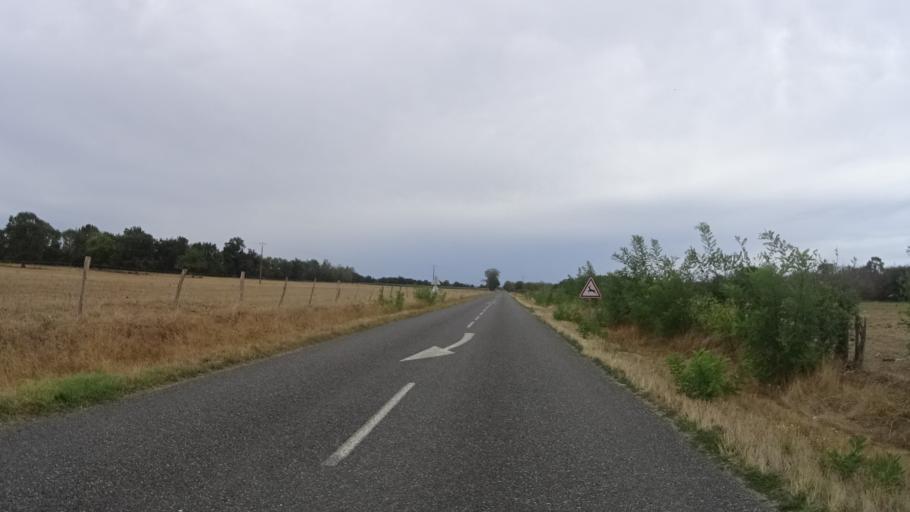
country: FR
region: Bourgogne
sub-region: Departement de la Nievre
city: Lucenay-les-Aix
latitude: 46.7631
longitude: 3.5613
